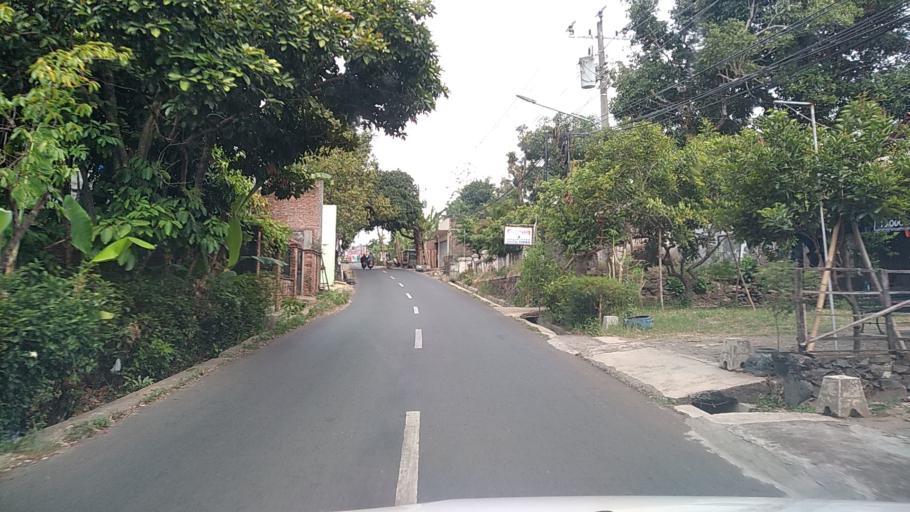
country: ID
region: Central Java
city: Semarang
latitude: -7.0132
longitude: 110.3343
